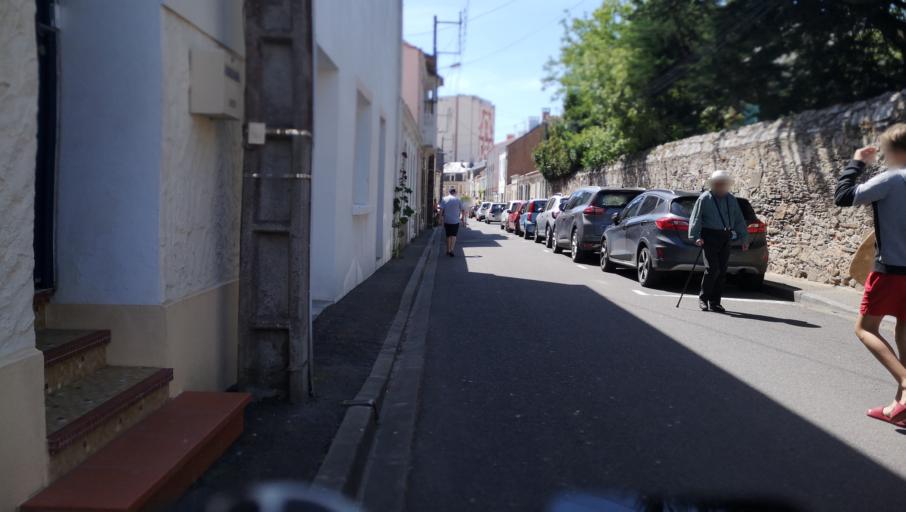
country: FR
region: Pays de la Loire
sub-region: Departement de la Vendee
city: Les Sables-d'Olonne
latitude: 46.4932
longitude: -1.7747
